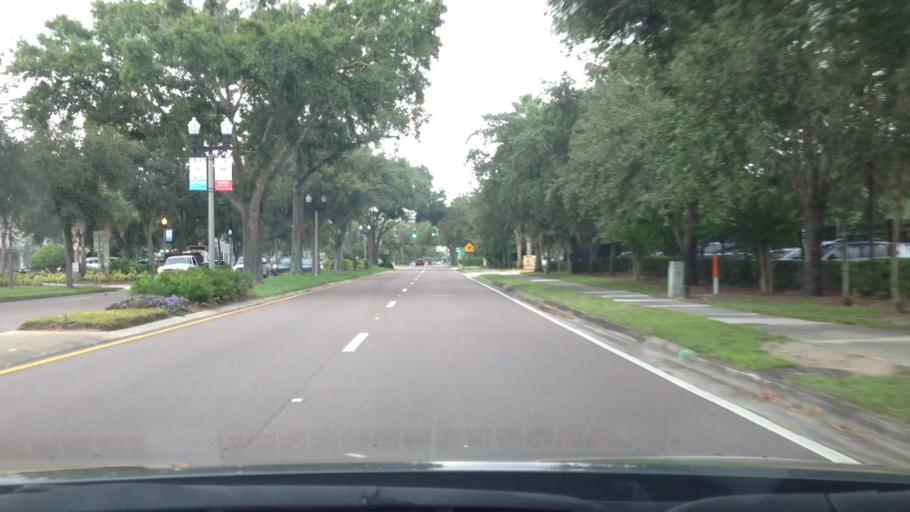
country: US
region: Florida
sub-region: Orange County
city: Maitland
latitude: 28.6344
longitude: -81.3657
